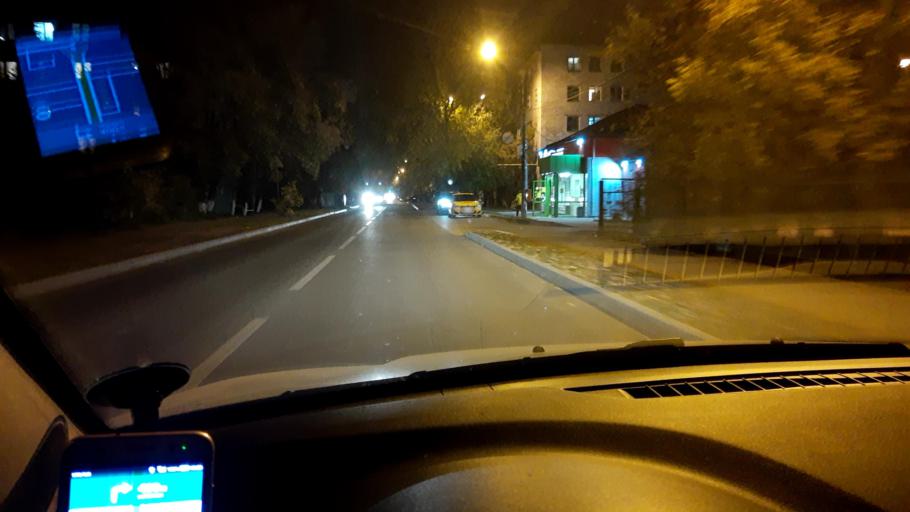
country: RU
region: Nizjnij Novgorod
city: Burevestnik
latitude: 56.2293
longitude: 43.8593
